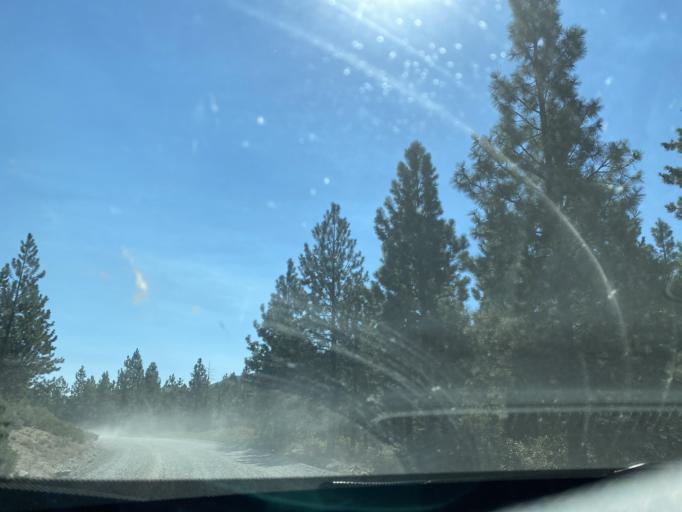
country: US
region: Oregon
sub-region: Deschutes County
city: Sunriver
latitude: 44.0331
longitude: -121.5513
